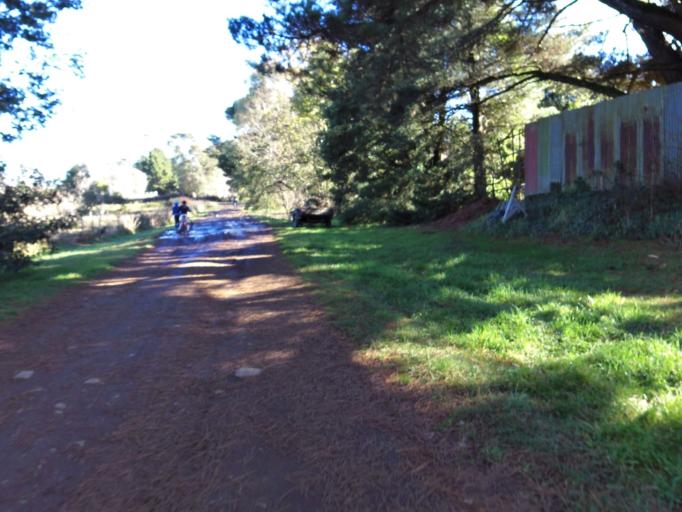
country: AU
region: Victoria
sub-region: Mount Alexander
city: Castlemaine
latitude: -37.3907
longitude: 144.2598
